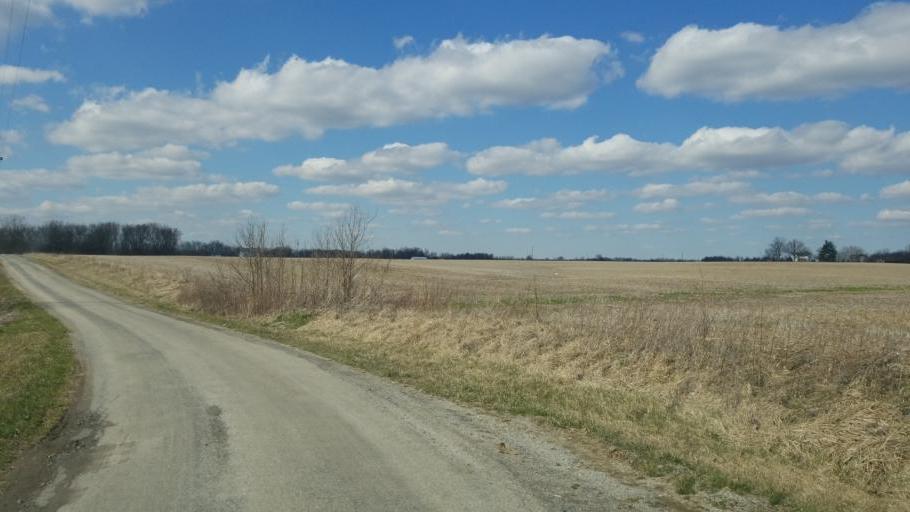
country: US
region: Ohio
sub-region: Highland County
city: Greenfield
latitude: 39.3014
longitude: -83.4237
